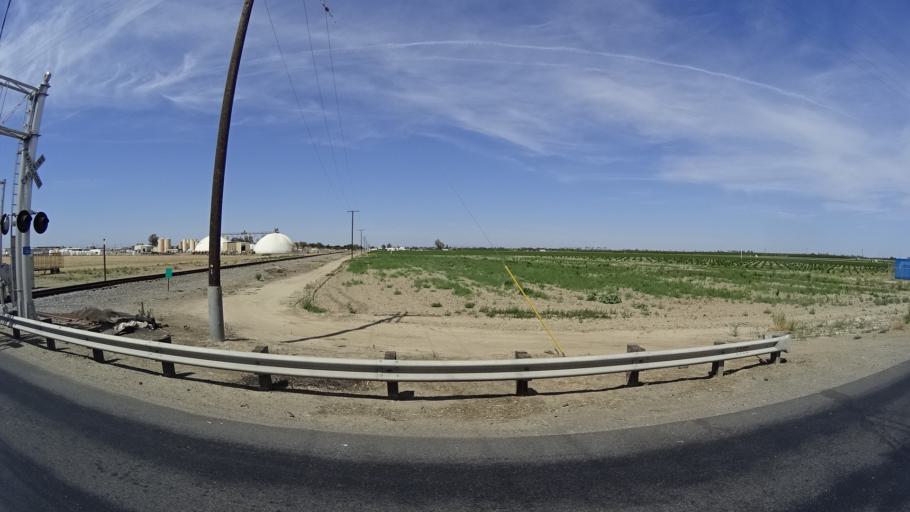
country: US
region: California
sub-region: Kings County
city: Hanford
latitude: 36.3322
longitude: -119.6010
